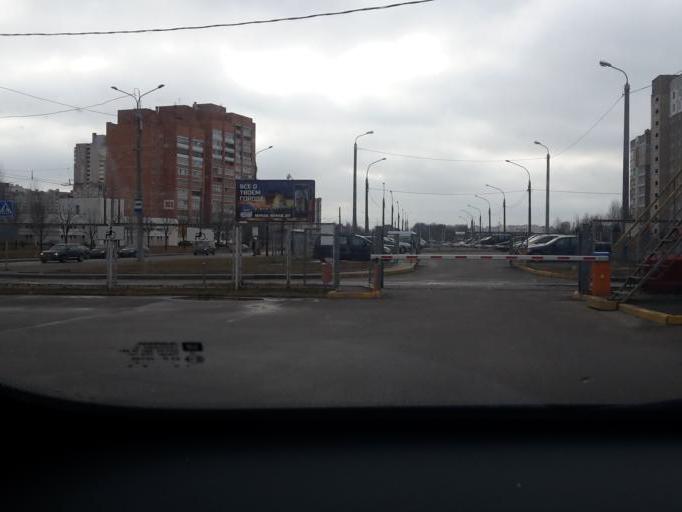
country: BY
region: Minsk
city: Novoye Medvezhino
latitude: 53.8839
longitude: 27.4305
